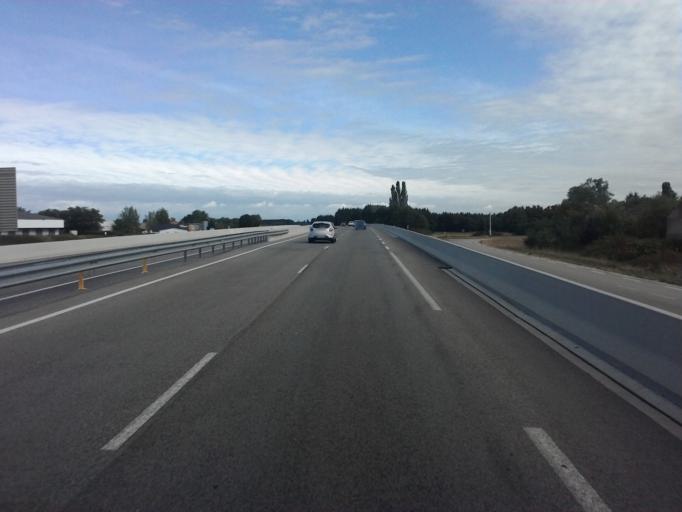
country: FR
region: Rhone-Alpes
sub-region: Departement de l'Ain
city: Certines
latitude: 46.1454
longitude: 5.2825
